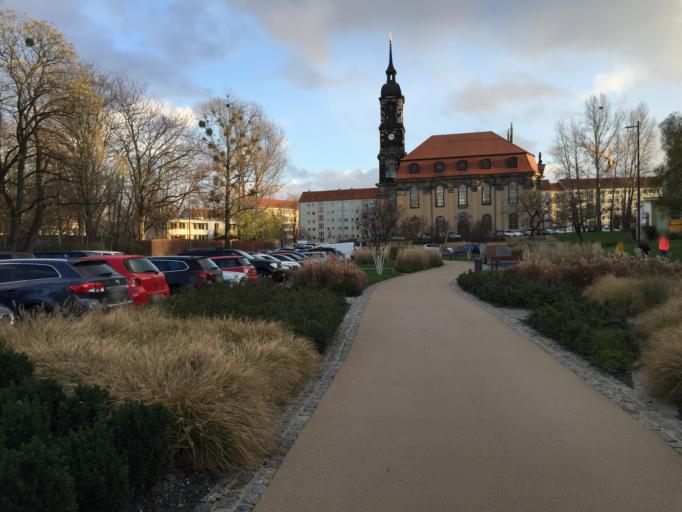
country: DE
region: Saxony
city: Dresden
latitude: 51.0497
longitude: 13.7257
